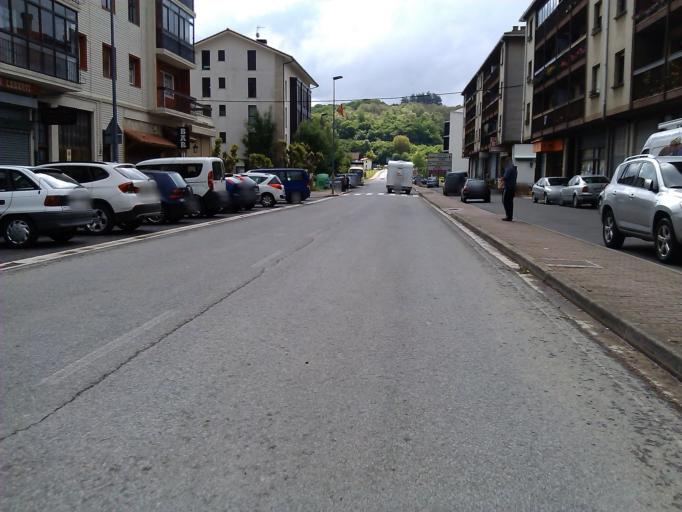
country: ES
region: Navarre
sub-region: Provincia de Navarra
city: Lekunberri
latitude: 43.0018
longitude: -1.8922
